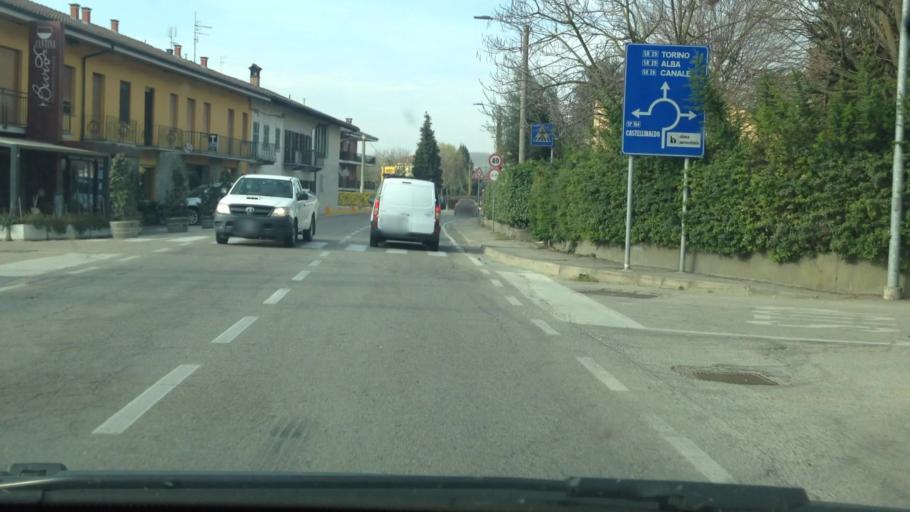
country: IT
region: Piedmont
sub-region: Provincia di Cuneo
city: Canale
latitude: 44.8041
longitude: 8.0216
